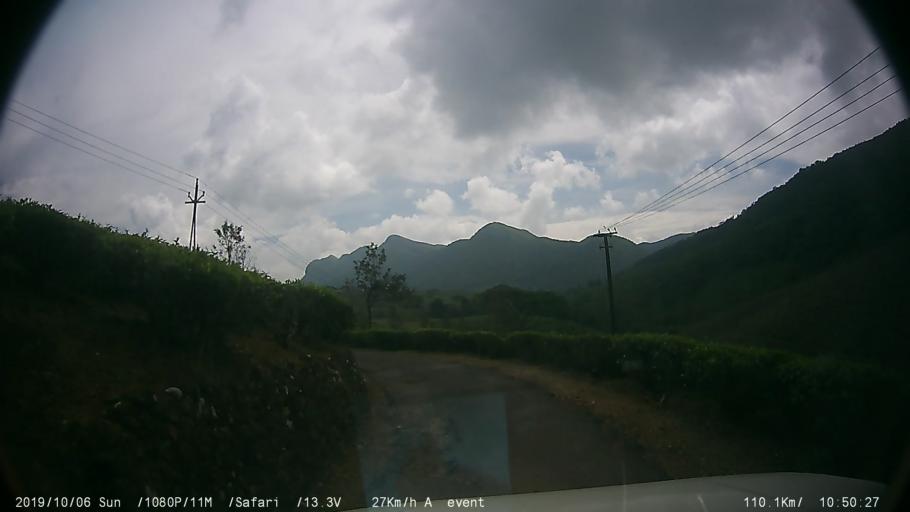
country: IN
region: Kerala
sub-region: Kottayam
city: Erattupetta
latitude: 9.6190
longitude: 76.9543
